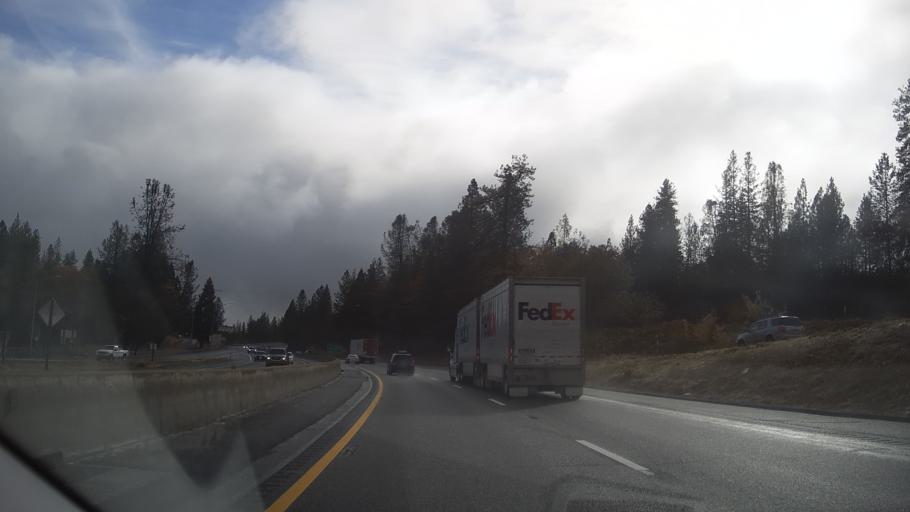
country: US
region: California
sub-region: Placer County
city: Colfax
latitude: 39.0438
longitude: -120.9743
